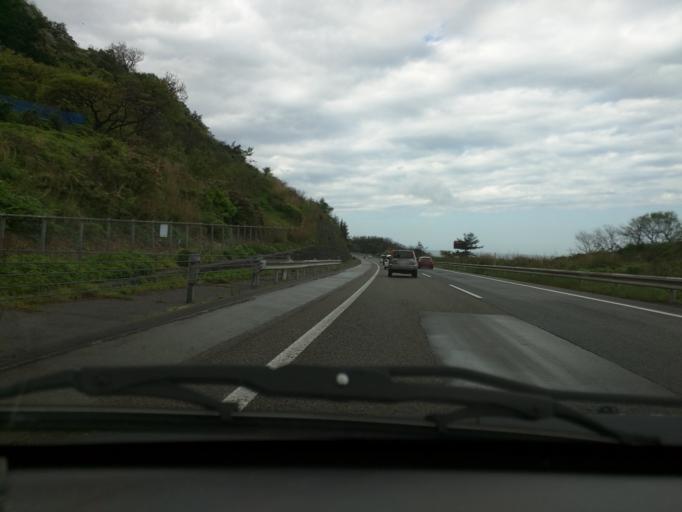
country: JP
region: Niigata
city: Kashiwazaki
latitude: 37.3131
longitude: 138.4306
